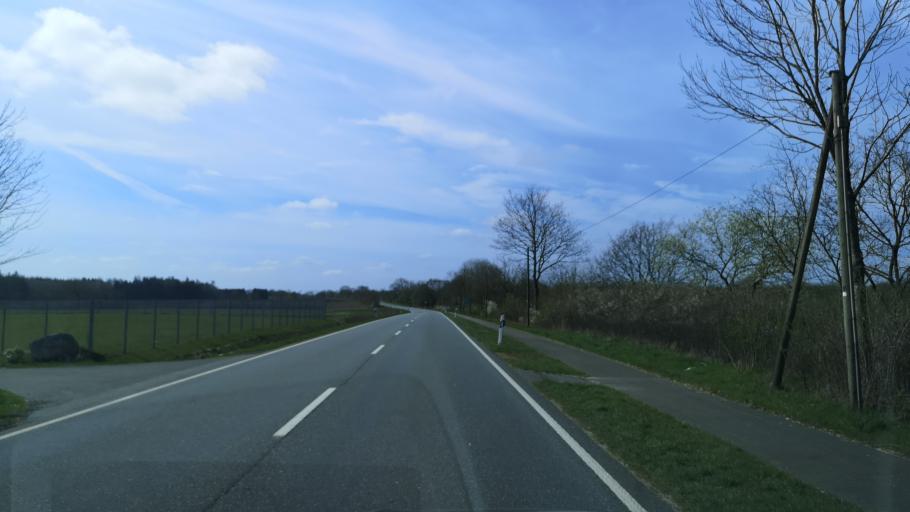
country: DE
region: Schleswig-Holstein
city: Albersdorf
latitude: 54.1246
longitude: 9.2735
